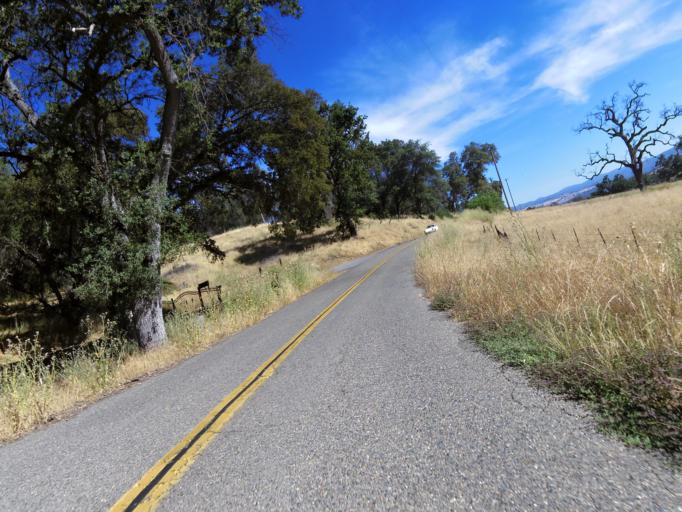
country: US
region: California
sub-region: Mariposa County
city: Mariposa
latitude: 37.3811
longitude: -119.9678
